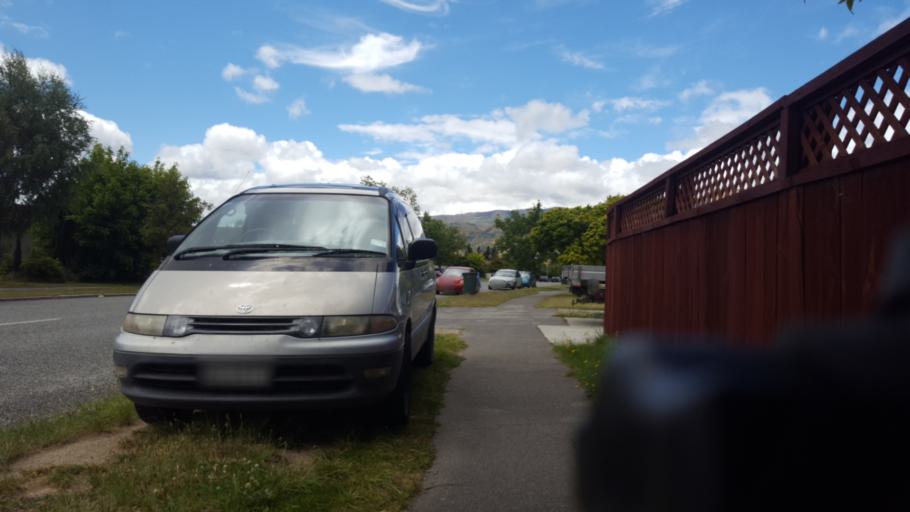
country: NZ
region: Otago
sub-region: Queenstown-Lakes District
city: Wanaka
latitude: -45.0395
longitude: 169.1841
